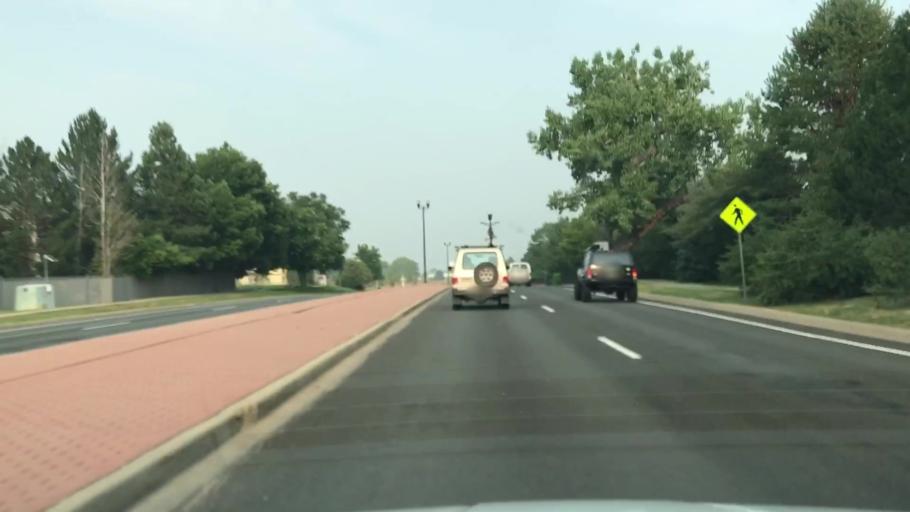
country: US
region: Colorado
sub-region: Boulder County
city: Louisville
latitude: 40.0001
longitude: -105.1186
